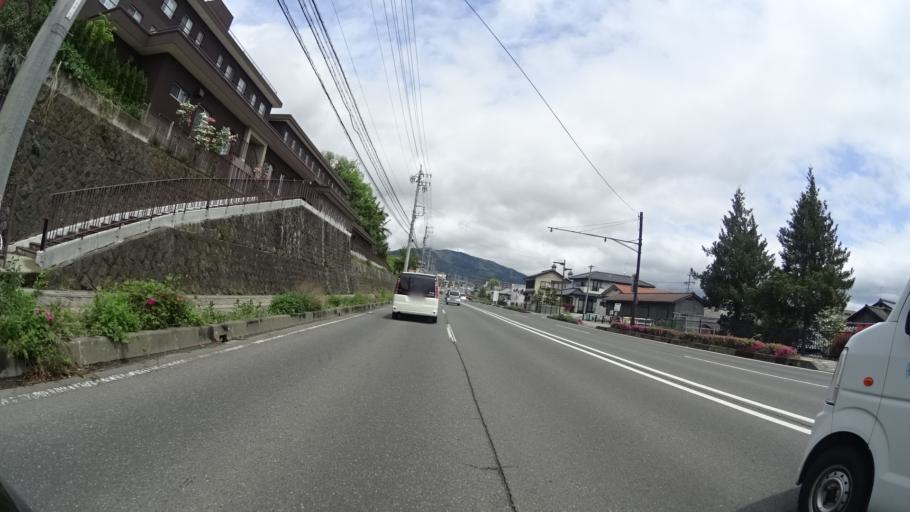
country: JP
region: Nagano
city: Nagano-shi
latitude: 36.6623
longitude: 138.1946
